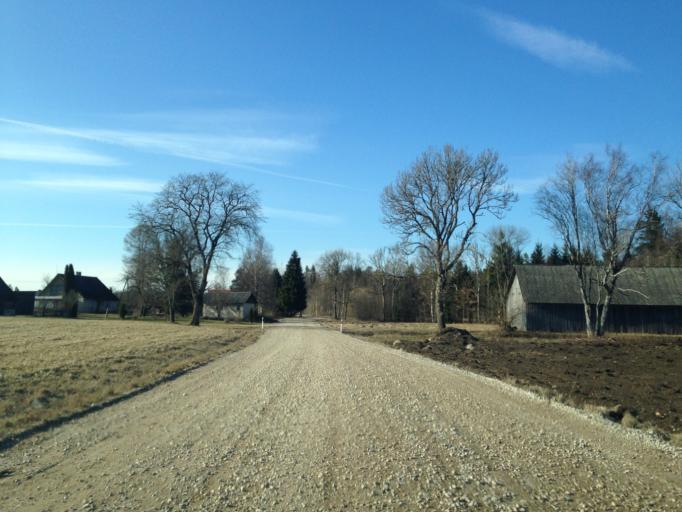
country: EE
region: Harju
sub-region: Nissi vald
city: Turba
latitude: 59.1647
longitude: 24.1424
